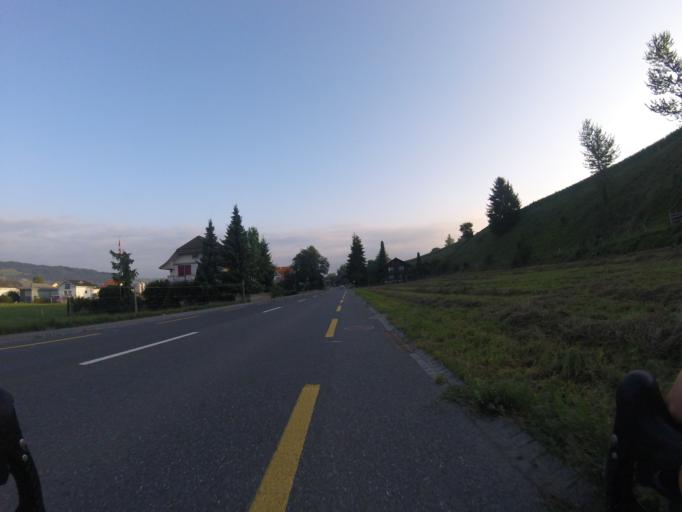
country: CH
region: Bern
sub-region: Bern-Mittelland District
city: Niederwichtrach
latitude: 46.8384
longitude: 7.5780
